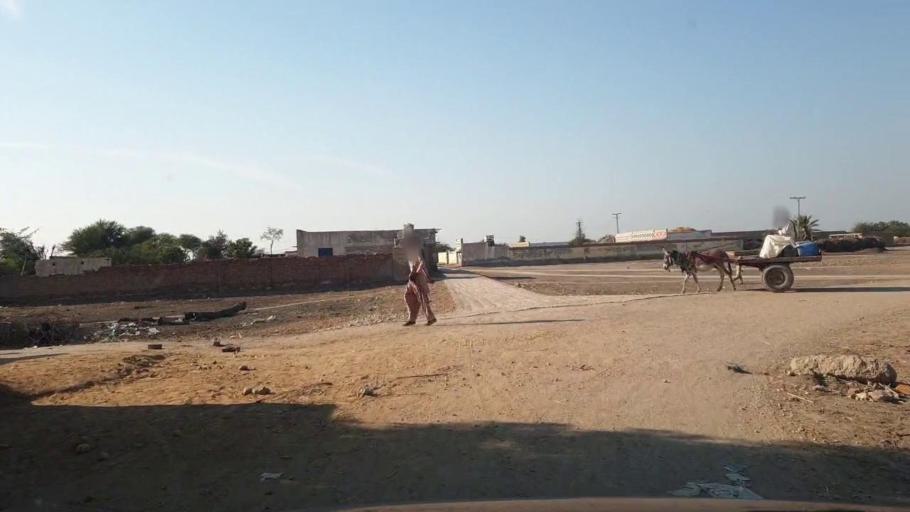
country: PK
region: Sindh
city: Shahpur Chakar
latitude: 26.1796
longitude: 68.6631
